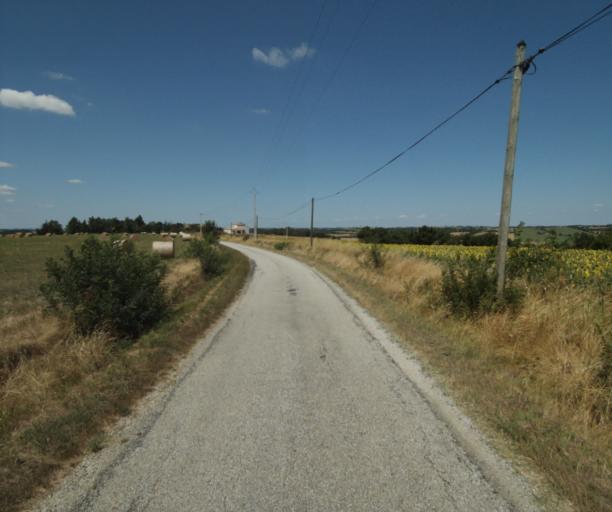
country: FR
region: Midi-Pyrenees
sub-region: Departement de la Haute-Garonne
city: Saint-Felix-Lauragais
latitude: 43.4794
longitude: 1.8682
